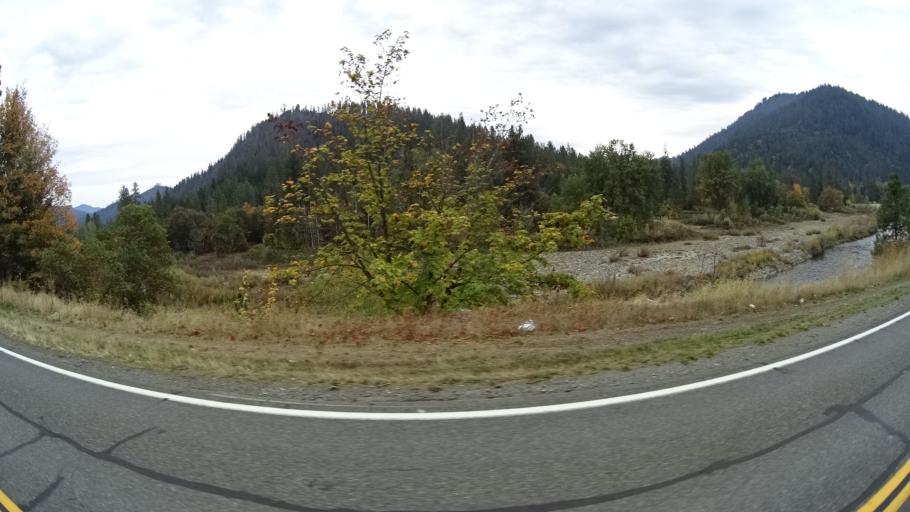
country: US
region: California
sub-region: Siskiyou County
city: Happy Camp
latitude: 41.7846
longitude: -123.3947
